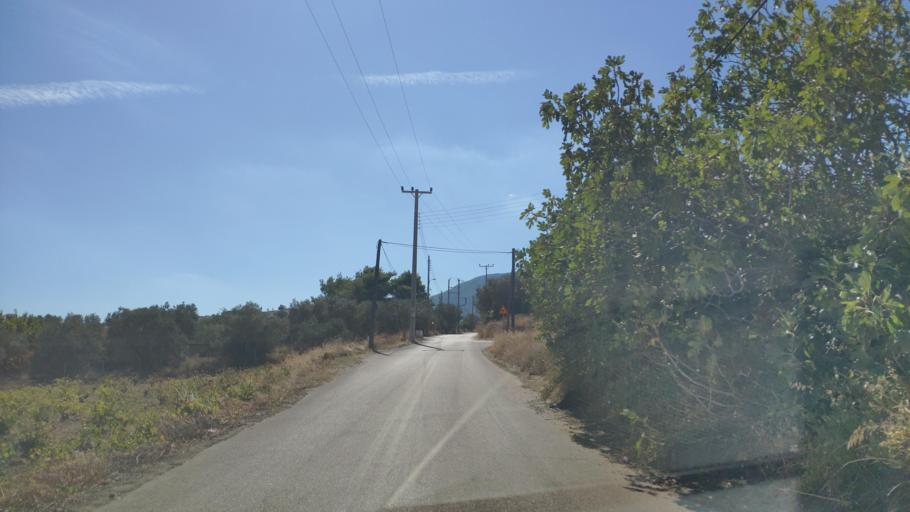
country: GR
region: Attica
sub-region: Nomarchia Anatolikis Attikis
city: Keratea
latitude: 37.8187
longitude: 23.9916
